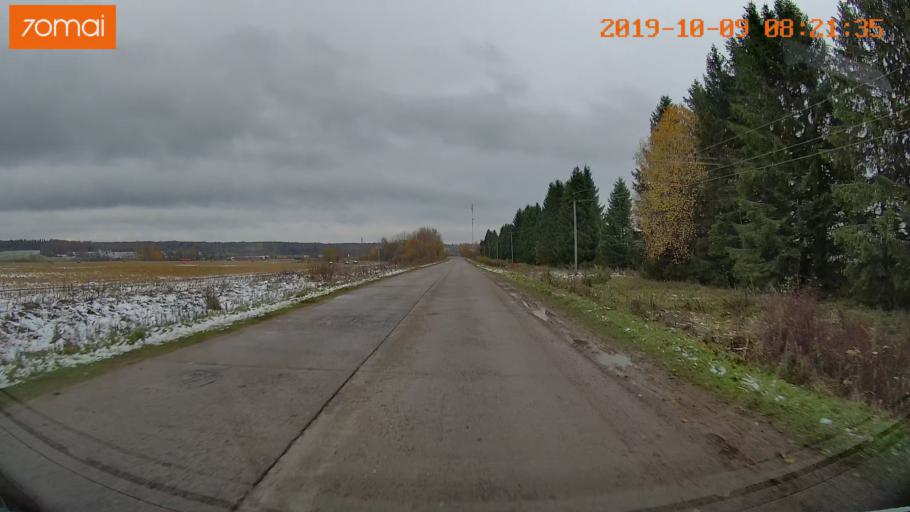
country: RU
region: Vologda
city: Gryazovets
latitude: 58.7420
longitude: 40.2793
